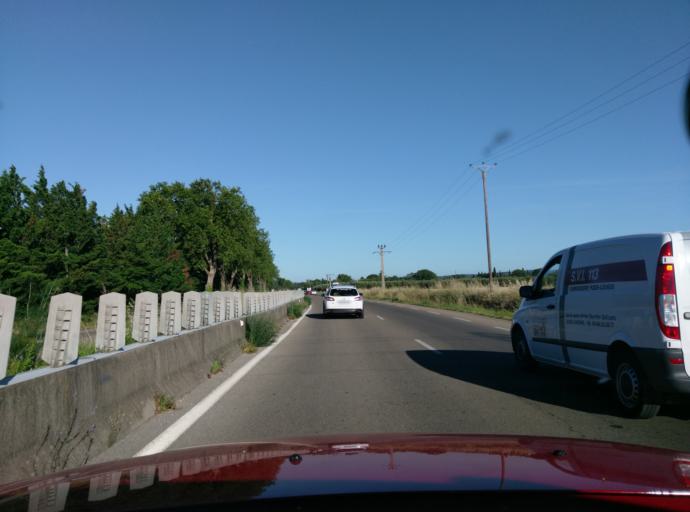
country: FR
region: Languedoc-Roussillon
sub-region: Departement du Gard
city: Rodilhan
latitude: 43.8311
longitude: 4.4487
